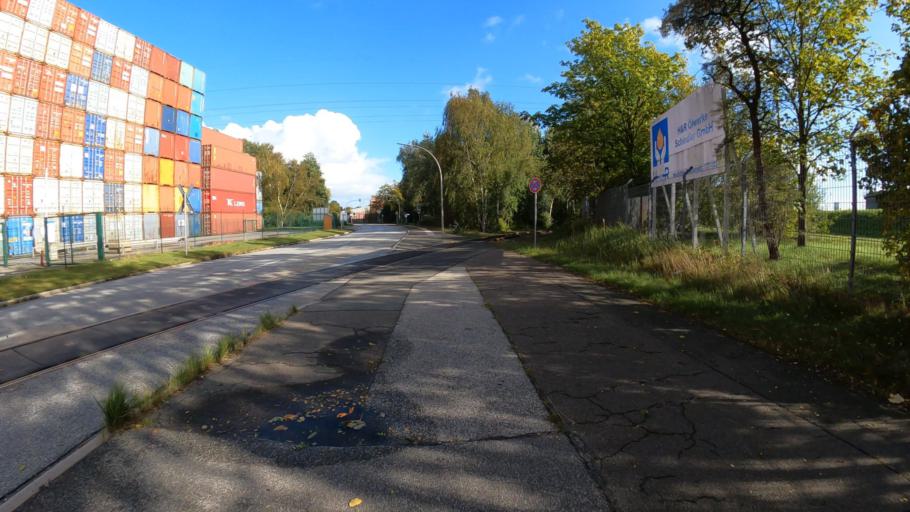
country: DE
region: Hamburg
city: Kleiner Grasbrook
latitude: 53.5124
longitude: 9.9646
